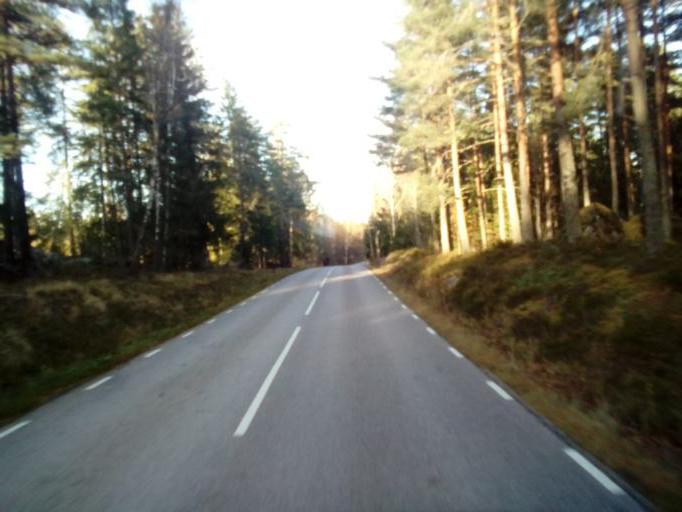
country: SE
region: Kalmar
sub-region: Vasterviks Kommun
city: Ankarsrum
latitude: 57.7672
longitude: 16.1374
